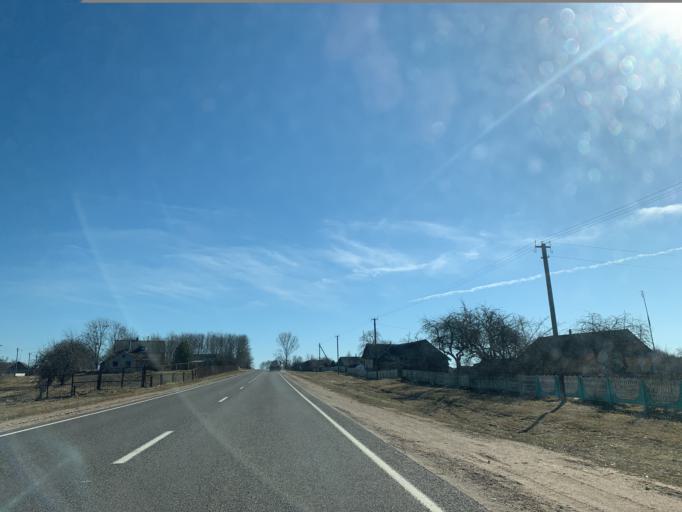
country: BY
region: Minsk
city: Nyasvizh
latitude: 53.2278
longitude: 26.7487
